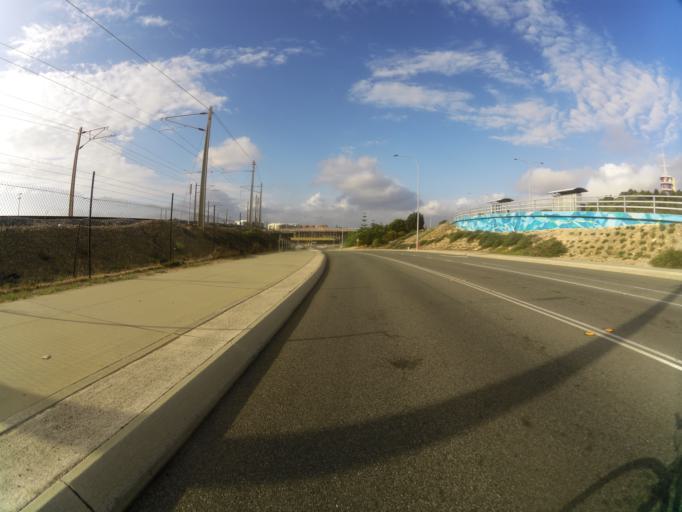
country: AU
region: Western Australia
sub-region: Fremantle
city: North Fremantle
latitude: -32.0437
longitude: 115.7533
